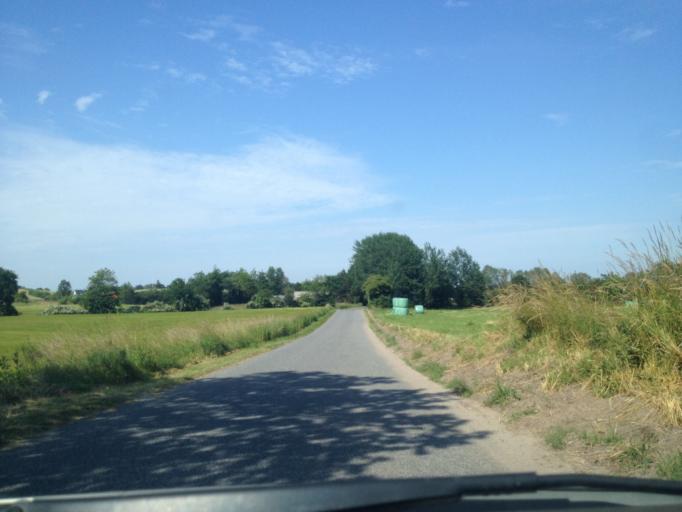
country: DK
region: Central Jutland
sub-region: Samso Kommune
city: Tranebjerg
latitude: 55.8442
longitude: 10.5614
